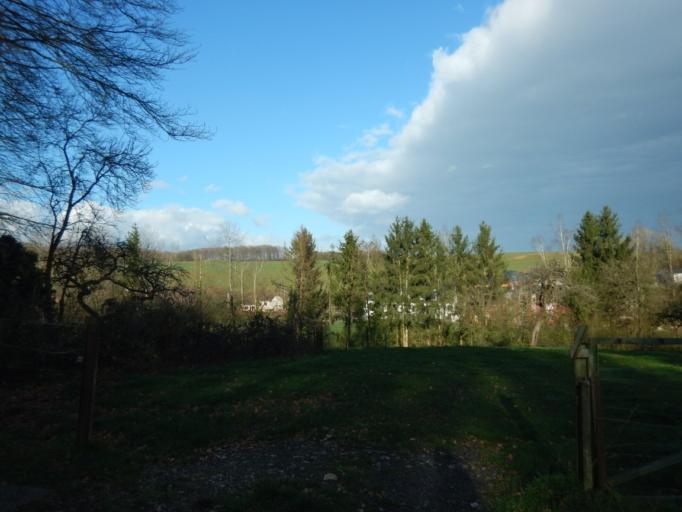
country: BE
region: Wallonia
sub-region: Province du Luxembourg
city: Attert
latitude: 49.7693
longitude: 5.8170
